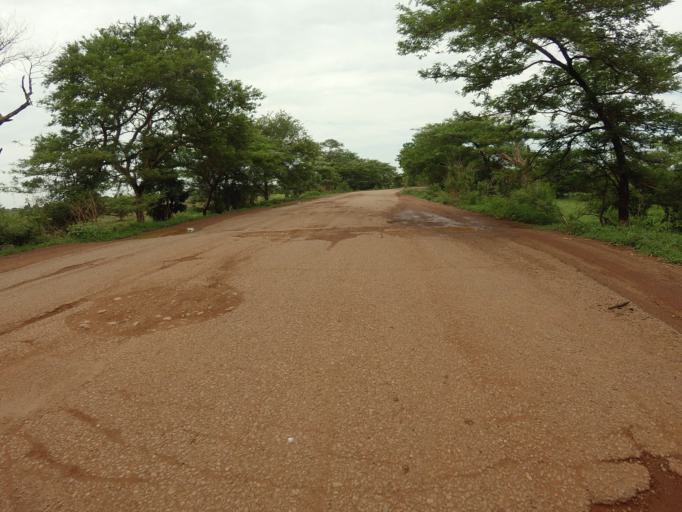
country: GH
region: Upper East
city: Bawku
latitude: 11.0026
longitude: -0.3906
